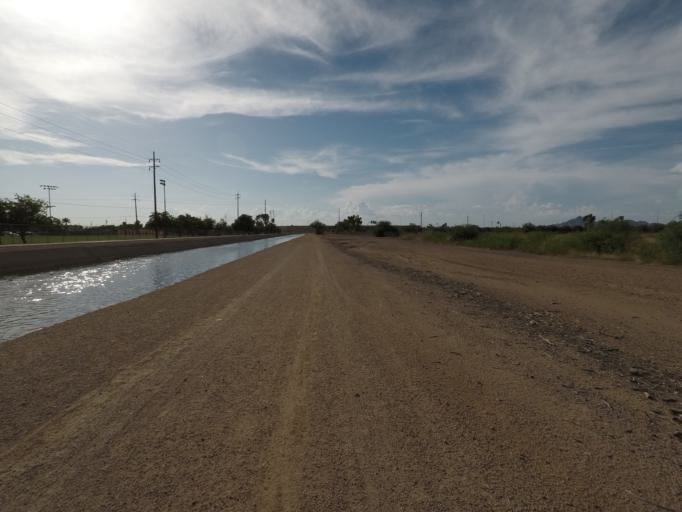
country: US
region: Arizona
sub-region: Maricopa County
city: Tempe Junction
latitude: 33.4558
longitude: -112.0020
